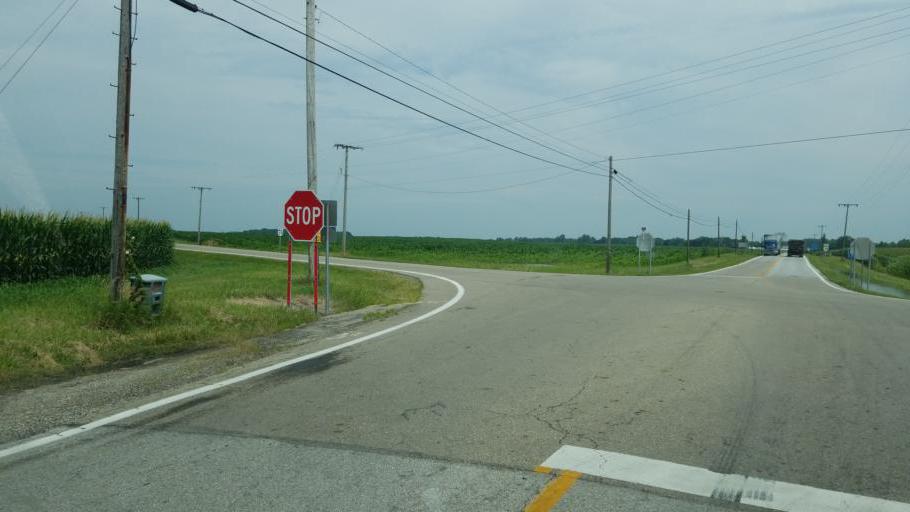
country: US
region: Ohio
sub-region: Madison County
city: Choctaw Lake
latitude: 39.9929
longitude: -83.4206
